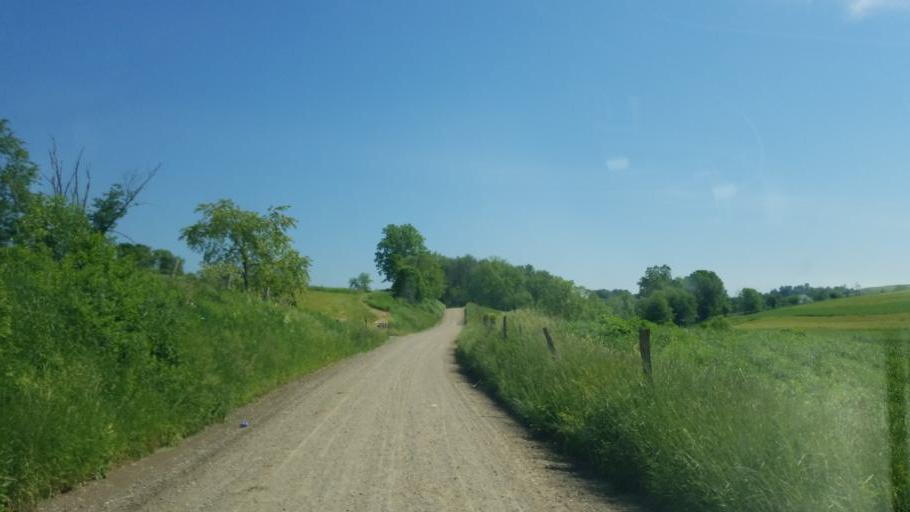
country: US
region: Ohio
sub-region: Holmes County
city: Millersburg
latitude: 40.4654
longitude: -81.7962
